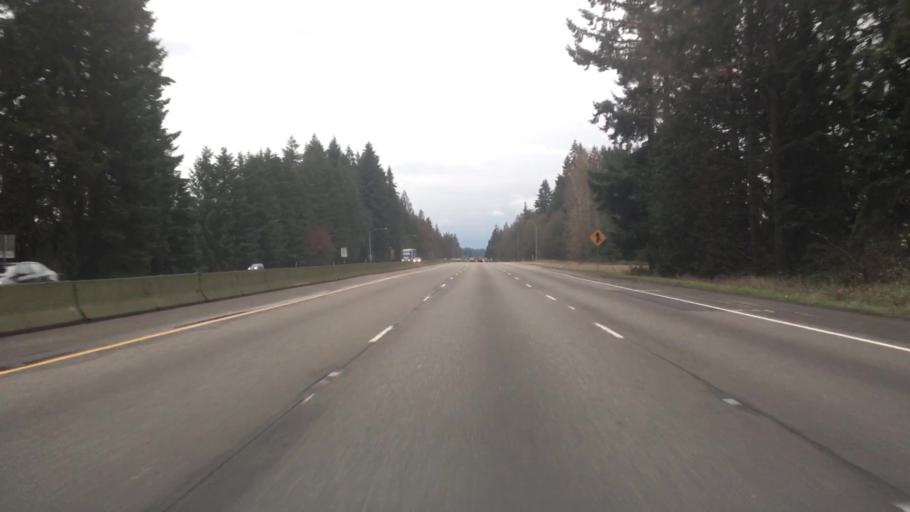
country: US
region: Washington
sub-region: Thurston County
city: Tumwater
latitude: 46.9513
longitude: -122.9380
